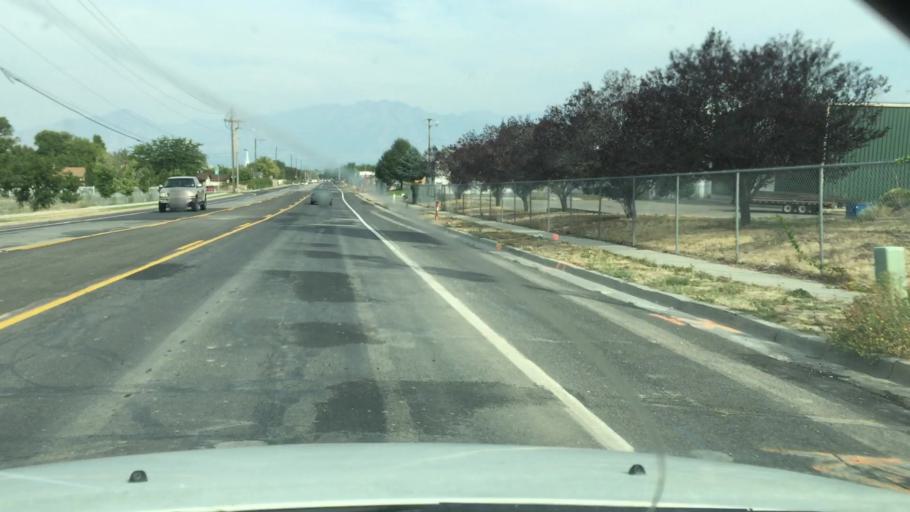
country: US
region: Utah
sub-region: Salt Lake County
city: Kearns
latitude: 40.6675
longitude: -112.0217
